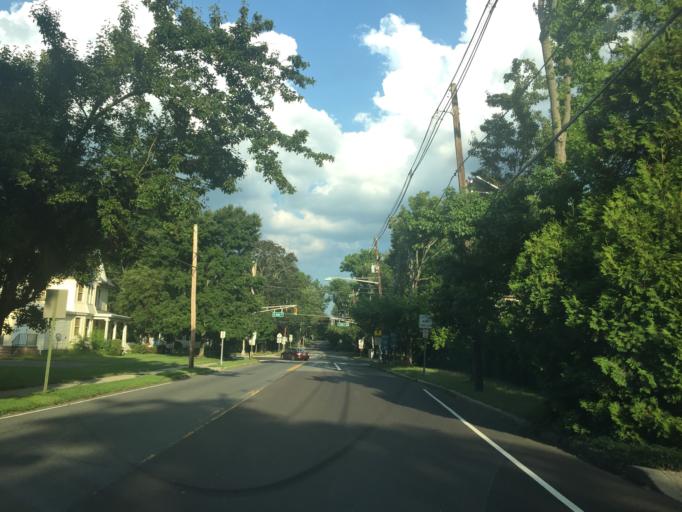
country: US
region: New Jersey
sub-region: Middlesex County
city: Cranbury
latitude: 40.3167
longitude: -74.5151
